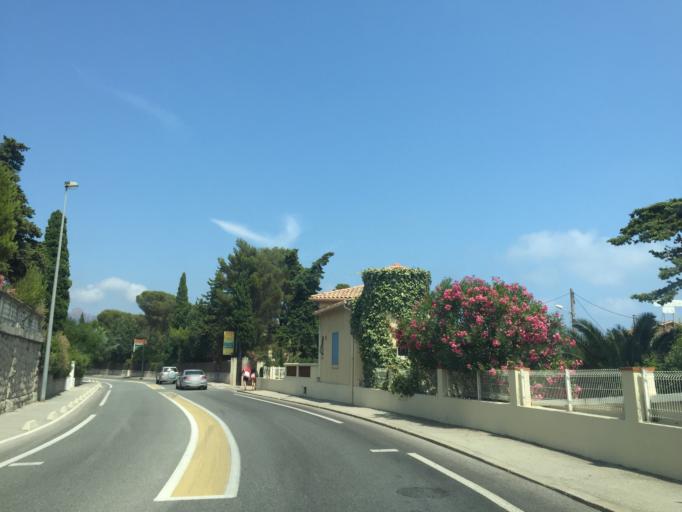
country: FR
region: Provence-Alpes-Cote d'Azur
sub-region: Departement du Var
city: Saint-Raphael
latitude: 43.4202
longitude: 6.8564
